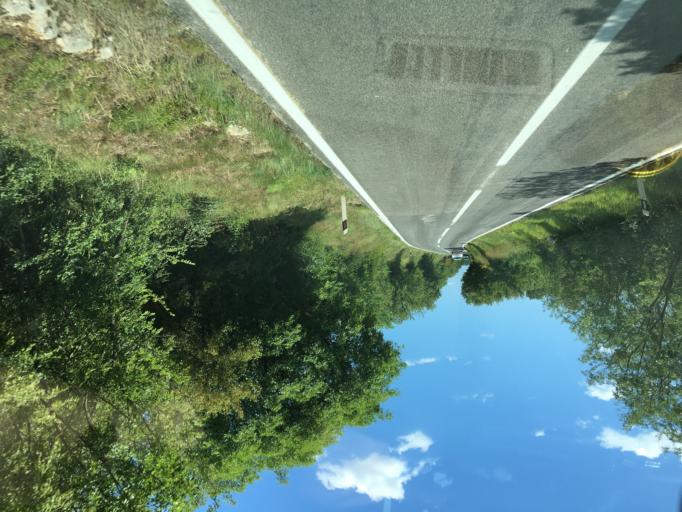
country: HR
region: Istarska
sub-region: Grad Rovinj
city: Rovinj
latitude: 45.1437
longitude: 13.7280
